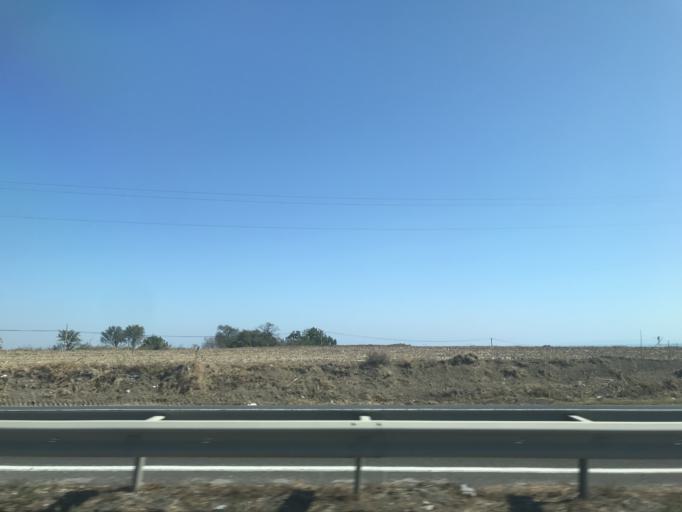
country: TR
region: Tekirdag
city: Tekirdag
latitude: 41.0159
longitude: 27.5182
